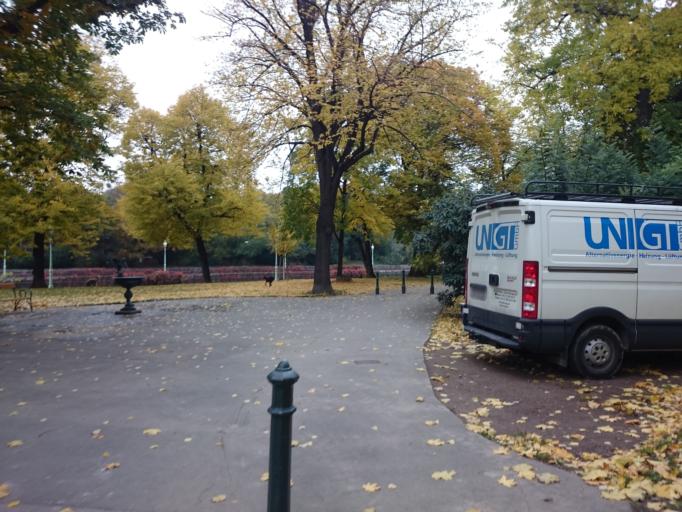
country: AT
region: Vienna
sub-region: Wien Stadt
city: Vienna
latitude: 48.2047
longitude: 16.3819
